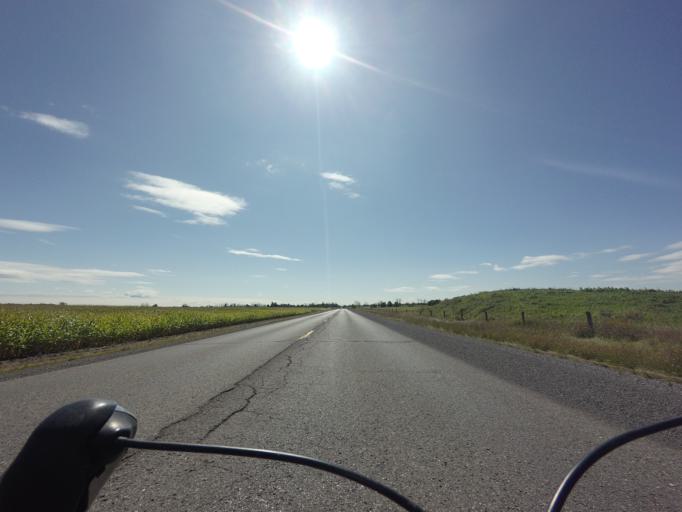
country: CA
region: Ontario
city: Bells Corners
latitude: 45.2200
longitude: -75.8312
